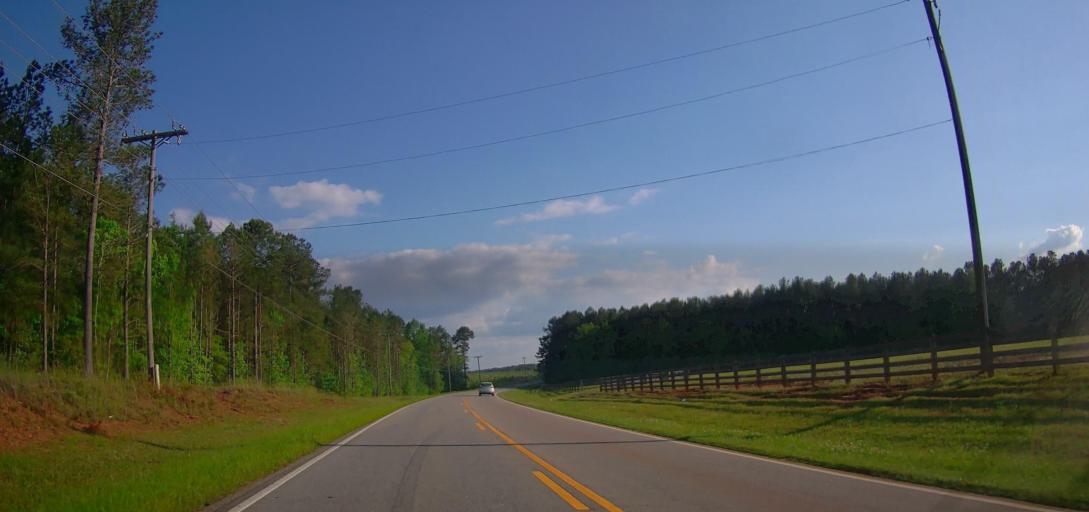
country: US
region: Georgia
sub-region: Putnam County
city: Eatonton
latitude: 33.2588
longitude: -83.3011
